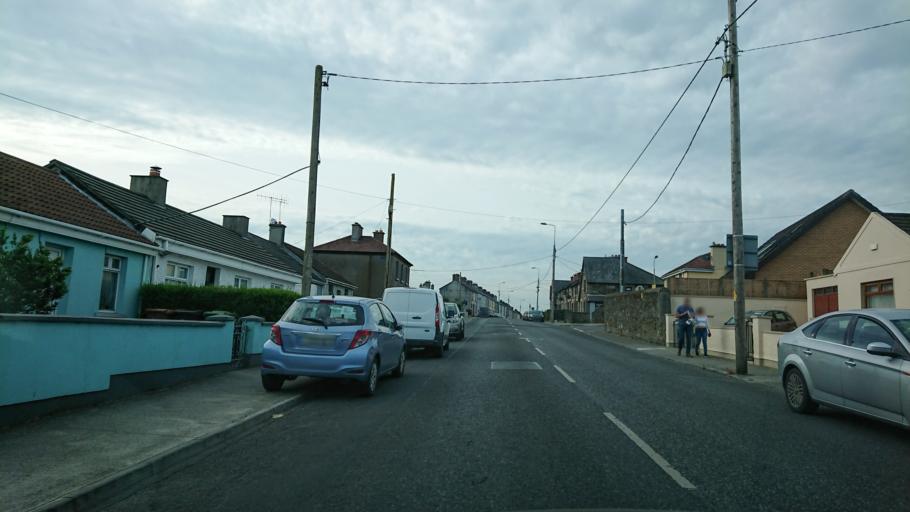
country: IE
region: Munster
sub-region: Waterford
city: Waterford
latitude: 52.2583
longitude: -7.1235
